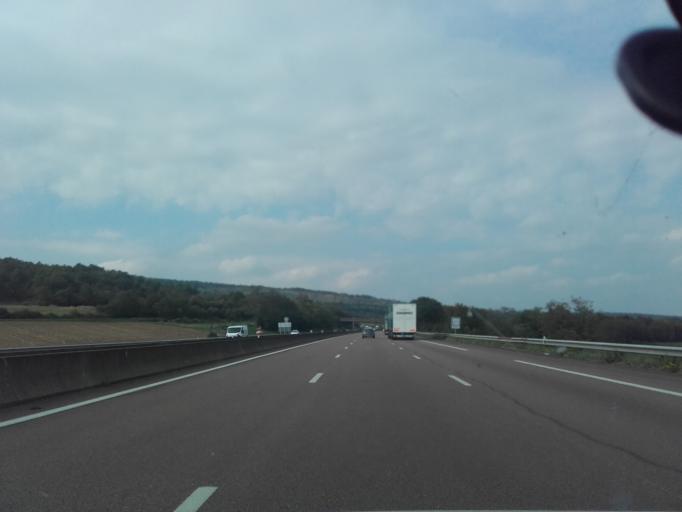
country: FR
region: Bourgogne
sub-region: Departement de Saone-et-Loire
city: Sennecey-le-Grand
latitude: 46.6142
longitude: 4.8695
